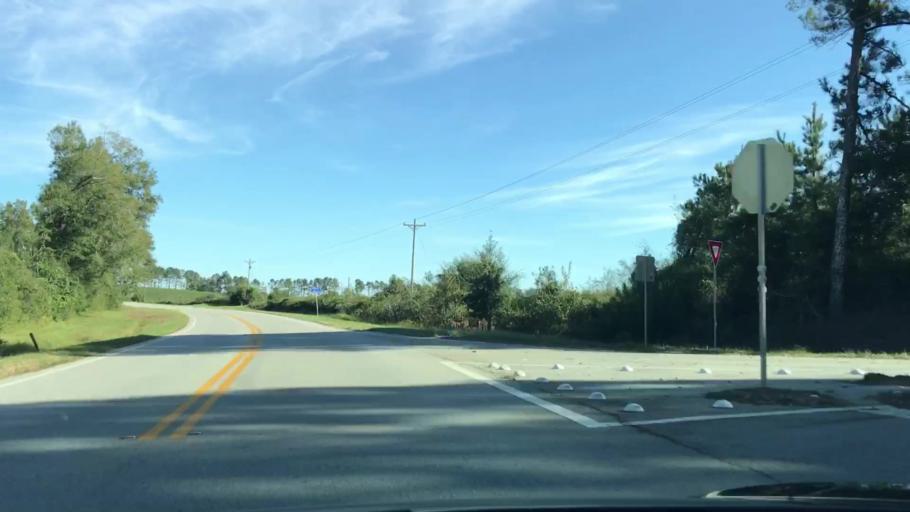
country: US
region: Georgia
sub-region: Glascock County
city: Gibson
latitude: 33.3201
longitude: -82.5567
